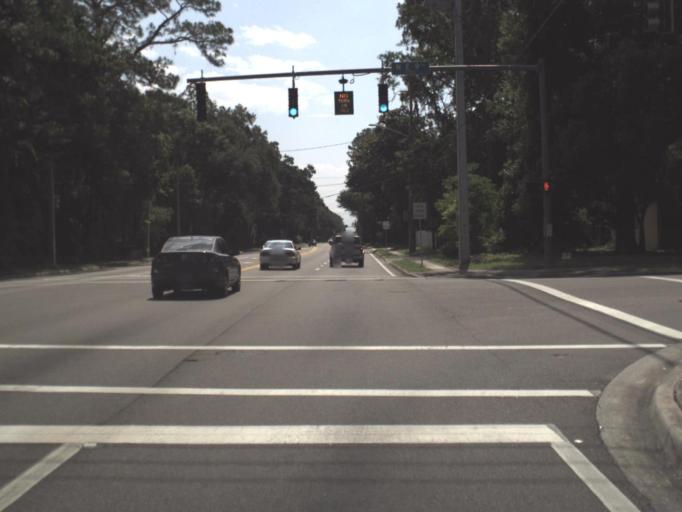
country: US
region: Florida
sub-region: Alachua County
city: Gainesville
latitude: 29.6738
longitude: -82.3150
